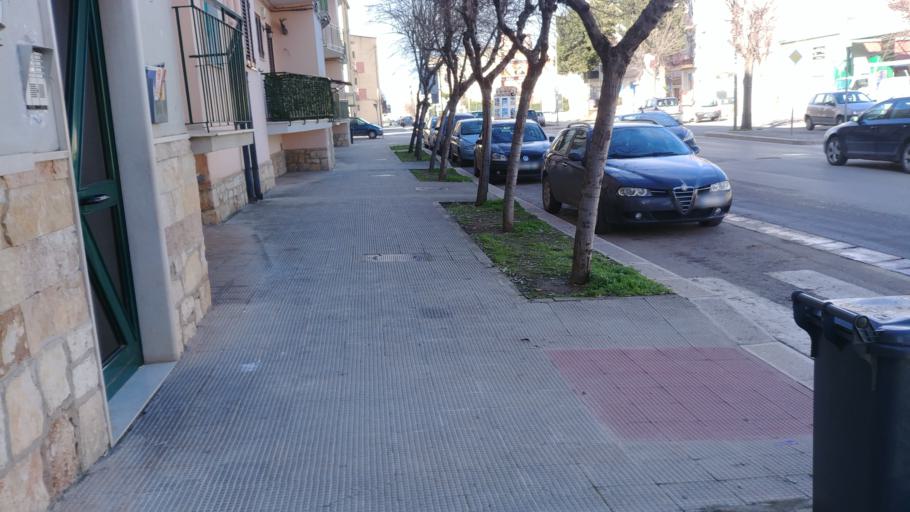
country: IT
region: Apulia
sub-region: Provincia di Barletta - Andria - Trani
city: Andria
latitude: 41.2363
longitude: 16.3064
